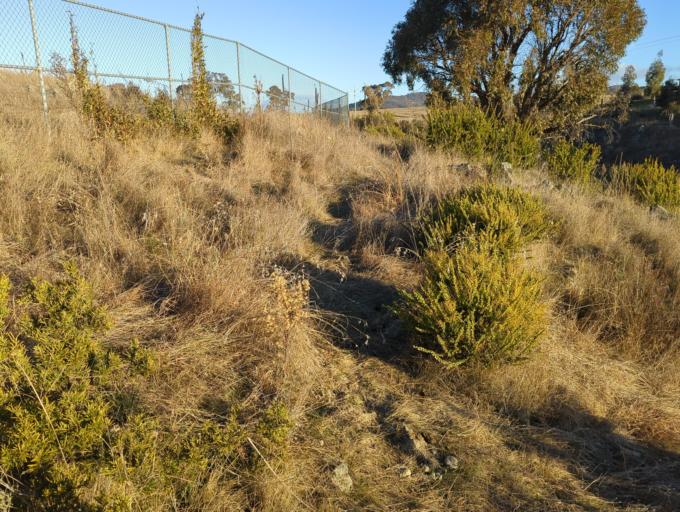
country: AU
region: New South Wales
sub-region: Queanbeyan
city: Queanbeyan
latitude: -35.4275
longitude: 149.2439
